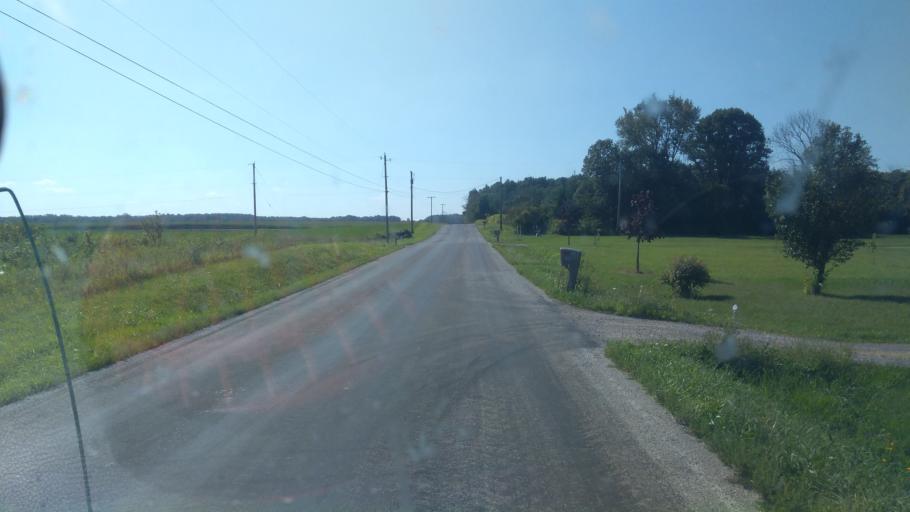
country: US
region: Ohio
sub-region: Ashland County
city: Ashland
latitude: 40.9699
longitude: -82.3065
